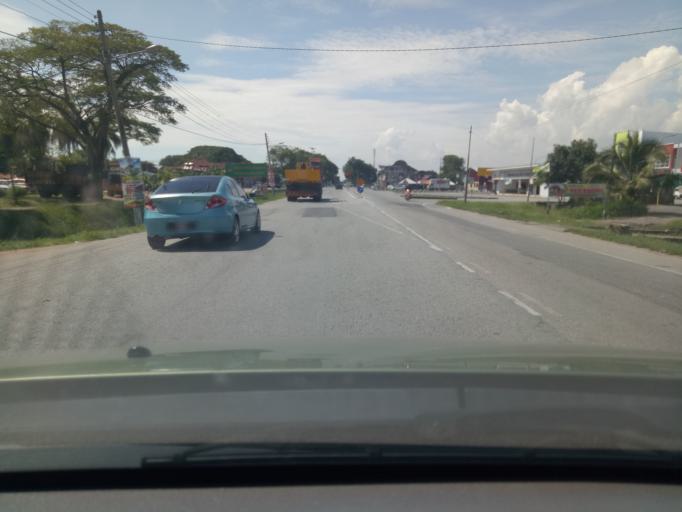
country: MY
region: Kedah
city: Alor Setar
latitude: 5.9721
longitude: 100.4007
